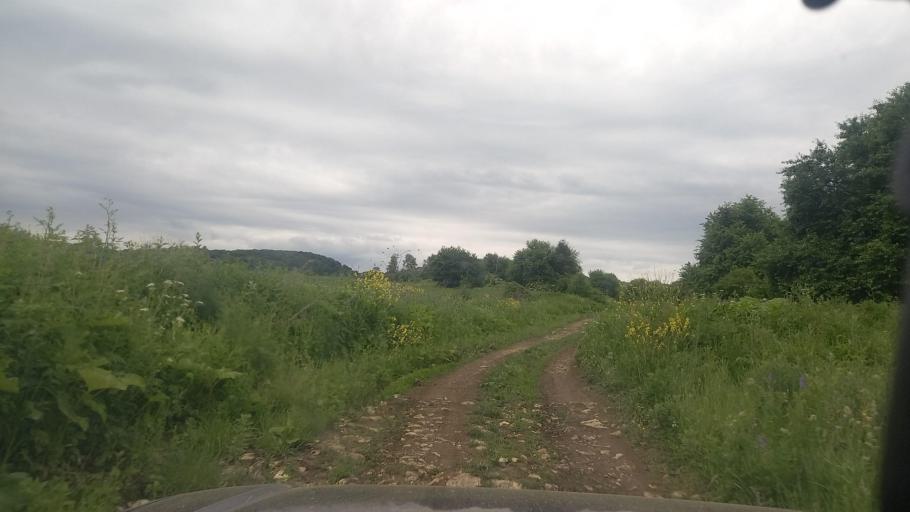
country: RU
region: Krasnodarskiy
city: Peredovaya
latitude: 44.0418
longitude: 41.3309
